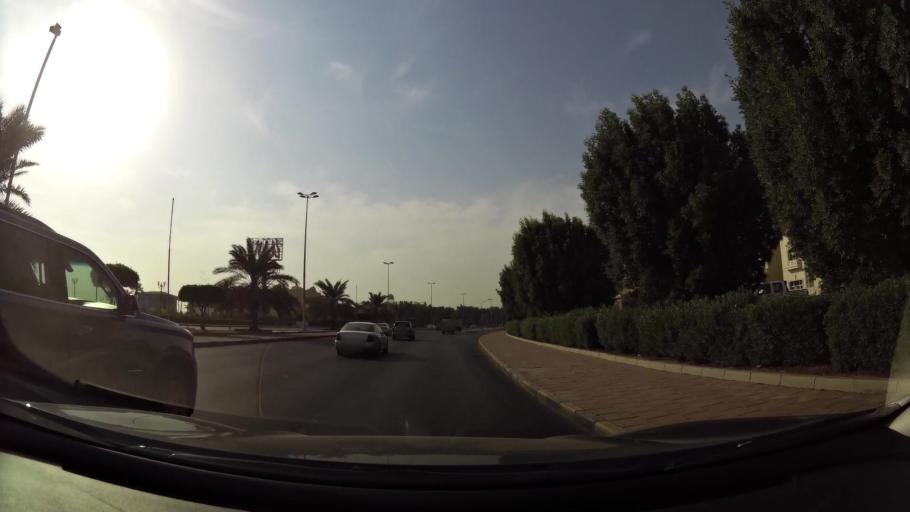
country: KW
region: Muhafazat Hawalli
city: Salwa
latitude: 29.2751
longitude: 48.0887
